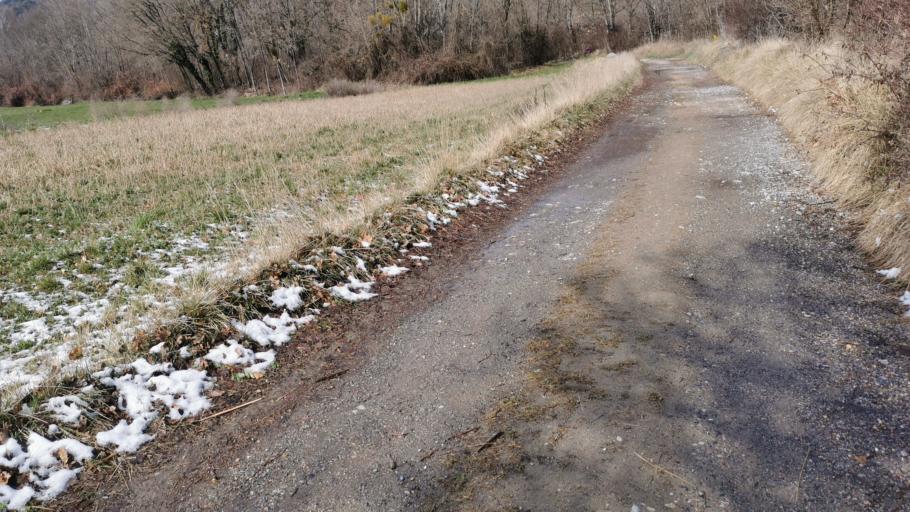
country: FR
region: Provence-Alpes-Cote d'Azur
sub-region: Departement des Alpes-de-Haute-Provence
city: Mallemoisson
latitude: 44.0617
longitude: 6.1763
